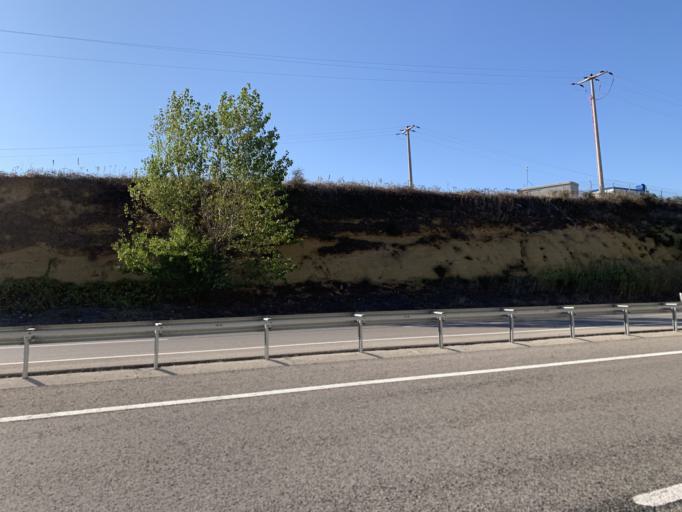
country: TR
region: Tekirdag
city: Inecik
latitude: 40.9607
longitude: 27.3579
